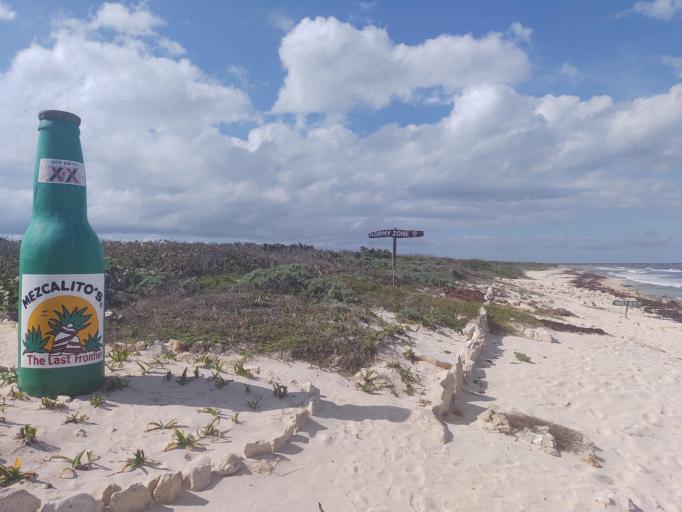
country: MX
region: Quintana Roo
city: San Miguel de Cozumel
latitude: 20.4239
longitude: -86.8427
